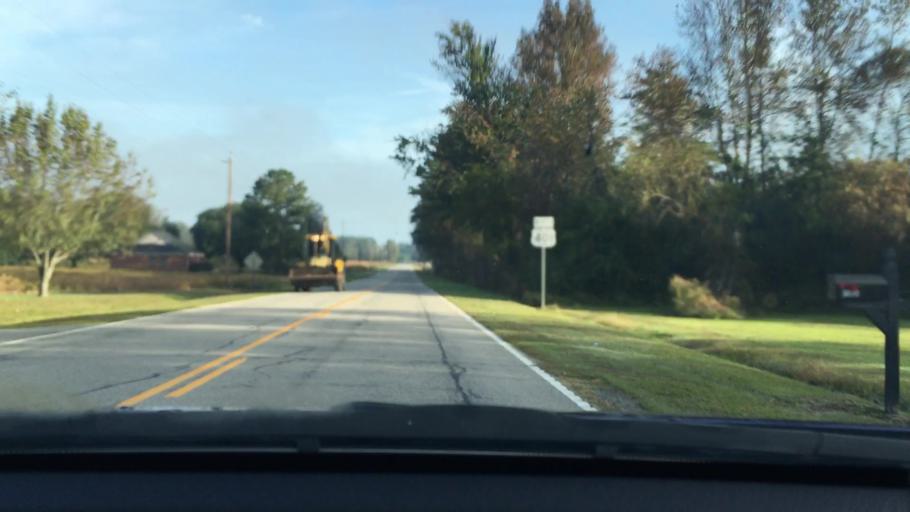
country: US
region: South Carolina
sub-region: Sumter County
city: East Sumter
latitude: 33.9987
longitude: -80.2889
